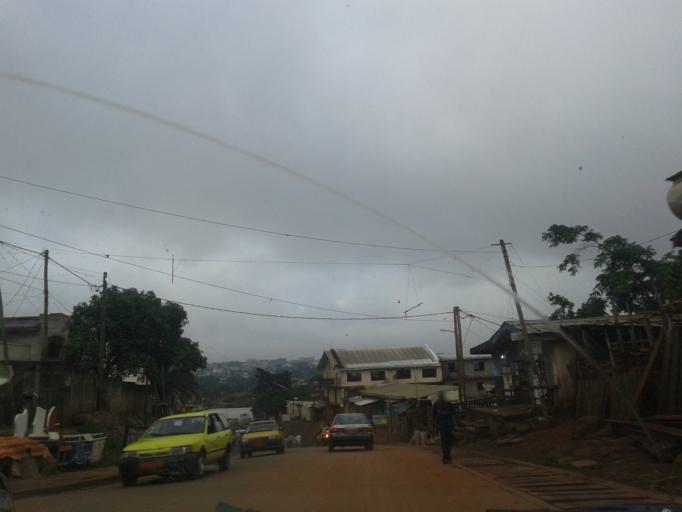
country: CM
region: Centre
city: Yaounde
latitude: 3.8887
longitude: 11.5300
